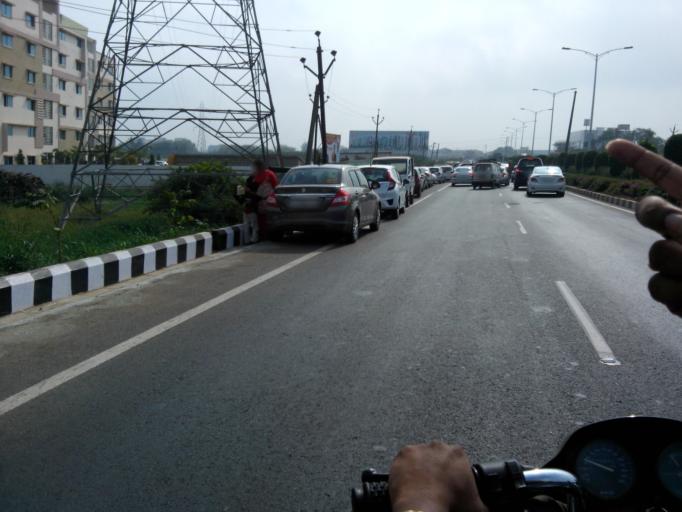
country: IN
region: Andhra Pradesh
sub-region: Krishna
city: Yanamalakuduru
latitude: 16.5233
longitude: 80.6686
